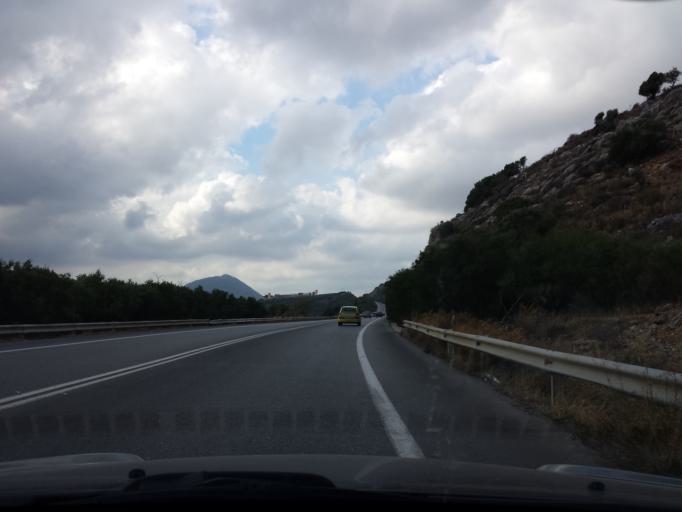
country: GR
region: Crete
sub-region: Nomos Lasithiou
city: Neapoli
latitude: 35.2516
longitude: 25.6224
